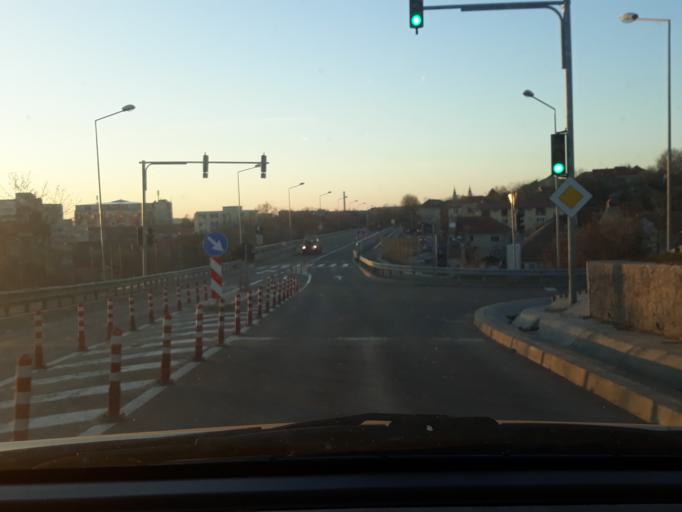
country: RO
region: Bihor
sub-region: Comuna Biharea
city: Oradea
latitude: 47.0609
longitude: 21.9443
